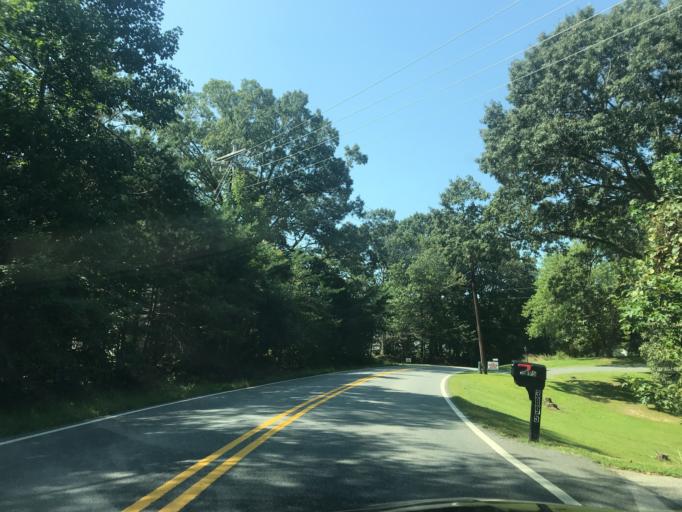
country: US
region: Maryland
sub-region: Calvert County
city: Prince Frederick
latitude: 38.4924
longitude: -76.6071
